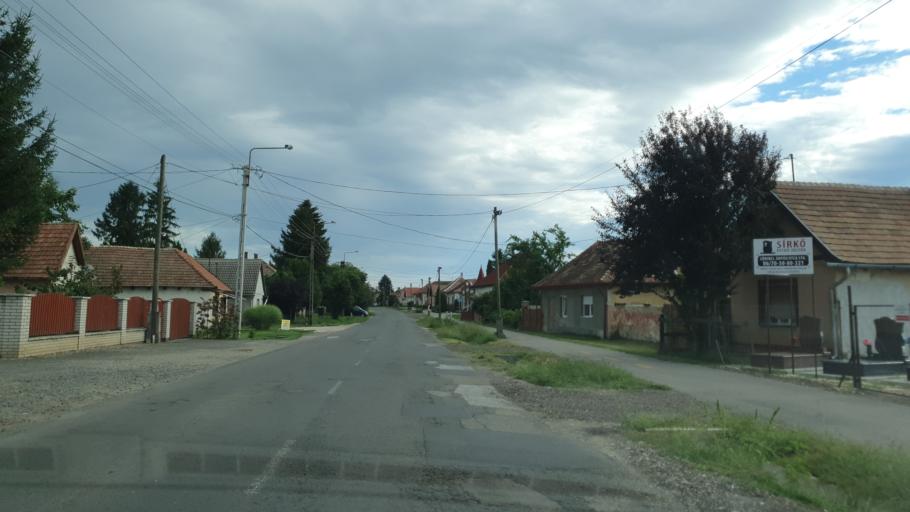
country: HU
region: Heves
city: Lorinci
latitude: 47.7506
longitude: 19.6797
